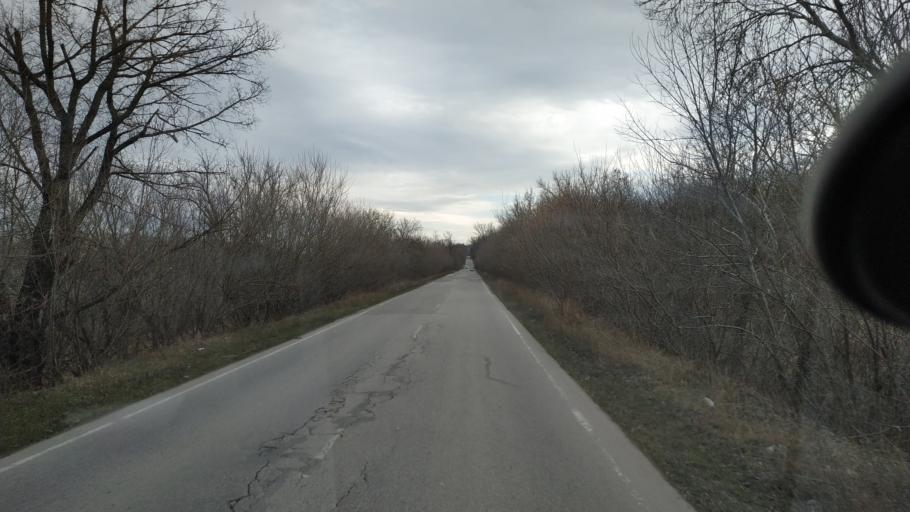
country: MD
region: Chisinau
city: Vadul lui Voda
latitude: 47.1098
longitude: 29.0613
